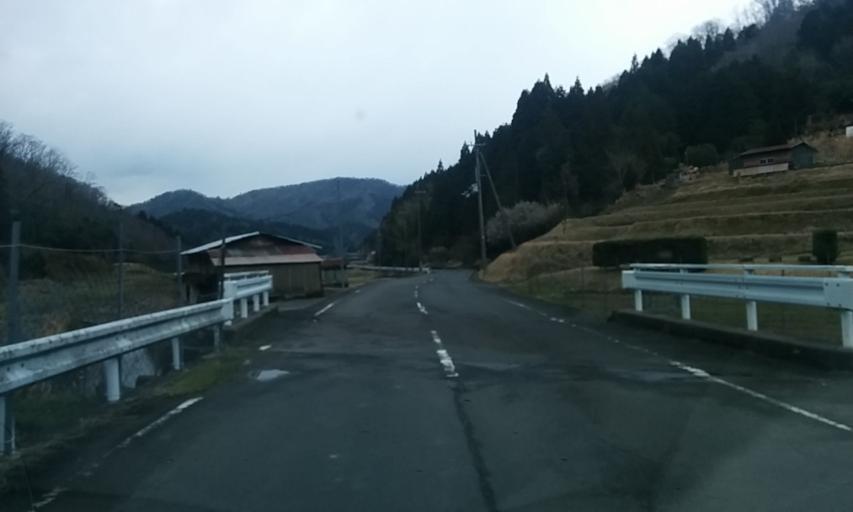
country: JP
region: Kyoto
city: Kameoka
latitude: 35.1205
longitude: 135.4193
